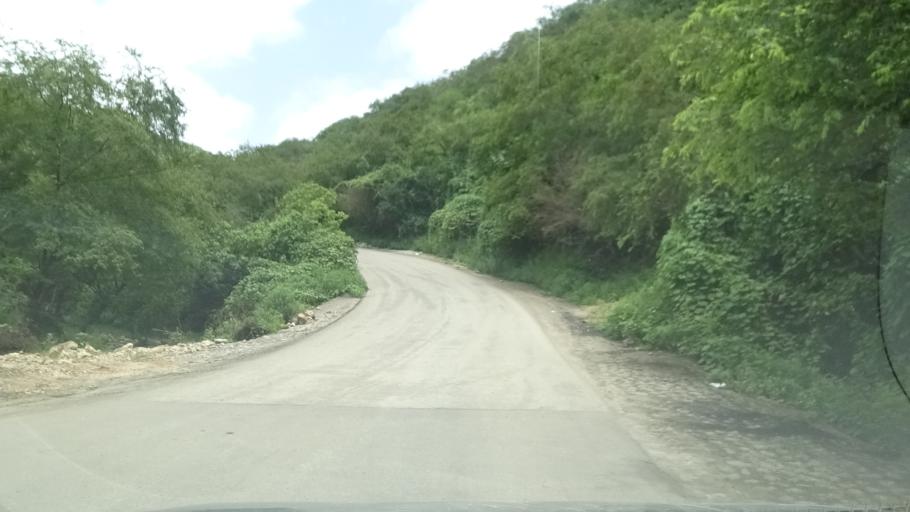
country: OM
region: Zufar
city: Salalah
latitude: 17.1635
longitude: 54.1691
